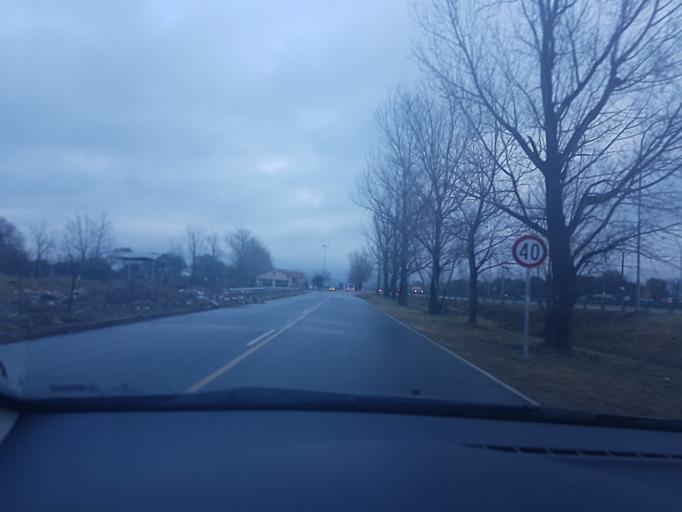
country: AR
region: Cordoba
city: Villa Allende
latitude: -31.3037
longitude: -64.2326
